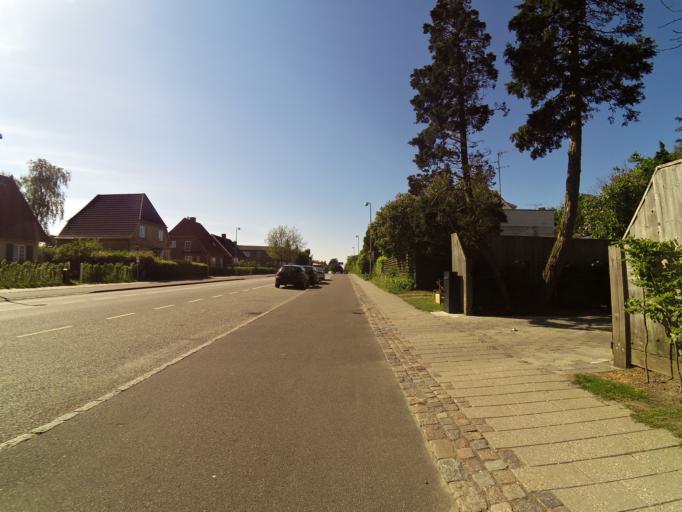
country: DK
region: Capital Region
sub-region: Gladsaxe Municipality
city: Buddinge
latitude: 55.7642
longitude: 12.4914
